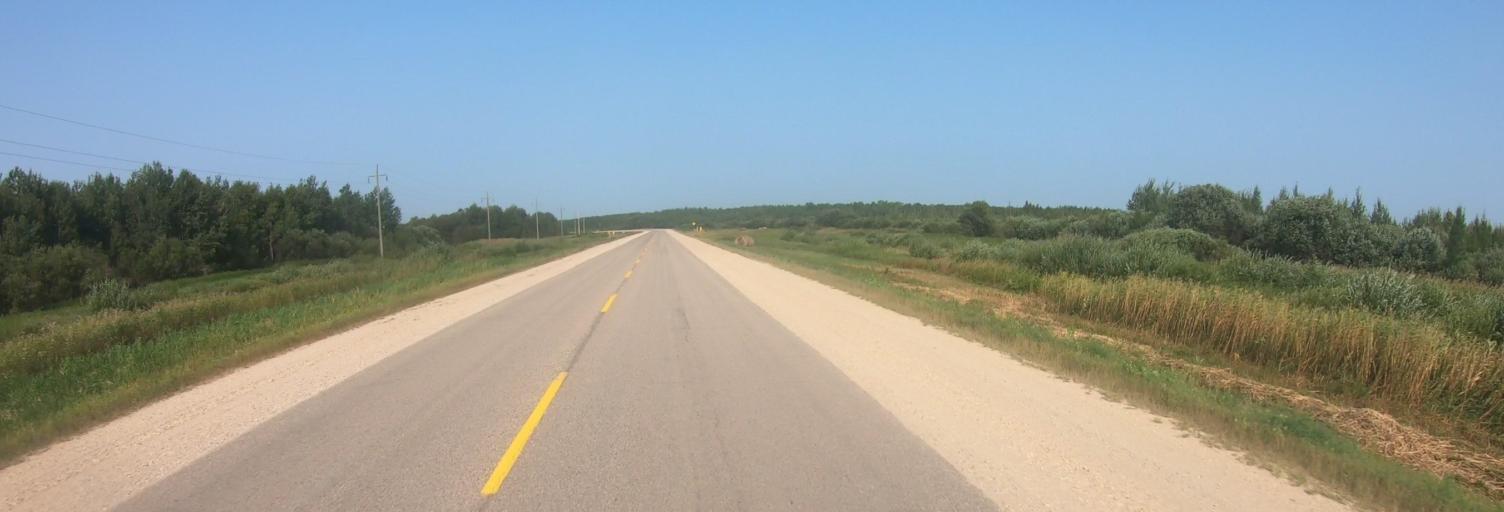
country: US
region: Minnesota
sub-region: Roseau County
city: Roseau
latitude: 49.0217
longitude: -95.5586
